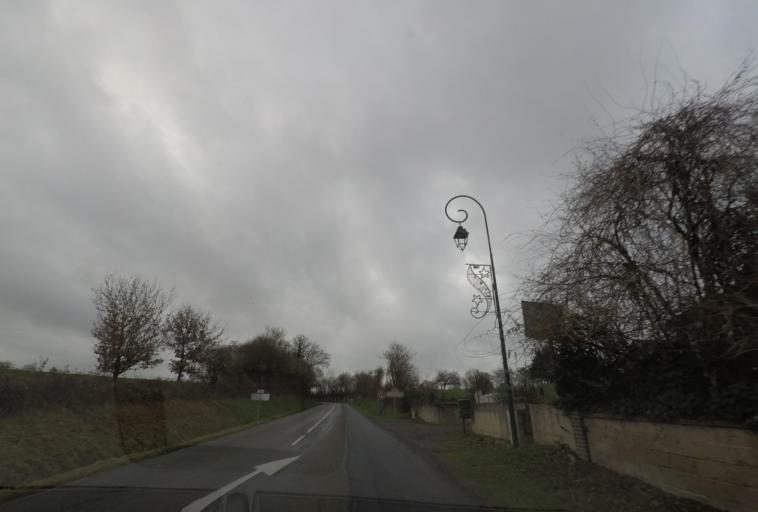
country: FR
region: Pays de la Loire
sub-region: Departement de la Sarthe
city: Vibraye
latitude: 47.9921
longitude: 0.7633
